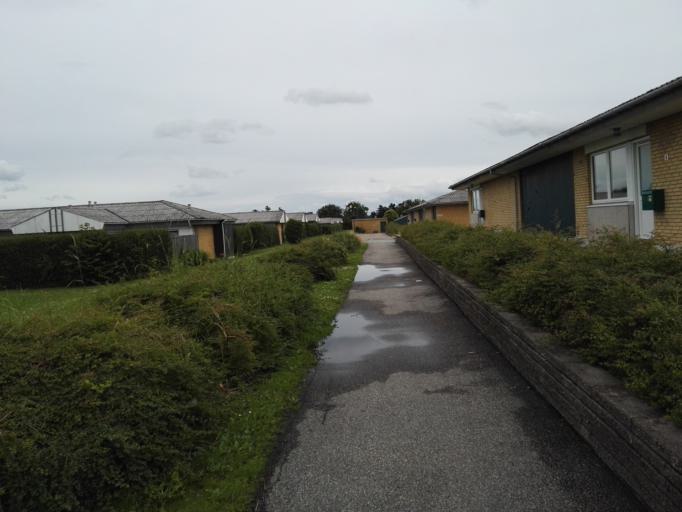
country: DK
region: Capital Region
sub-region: Egedal Kommune
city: Olstykke
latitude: 55.7757
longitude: 12.1682
